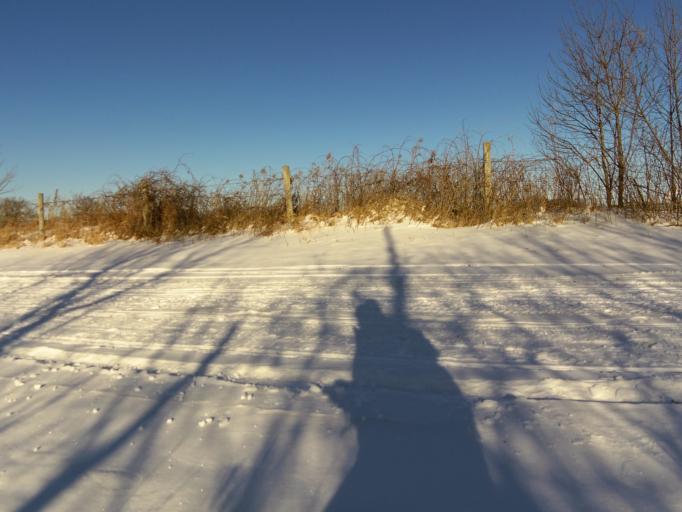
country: US
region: Minnesota
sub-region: Washington County
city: Lake Elmo
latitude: 44.9909
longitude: -92.9124
